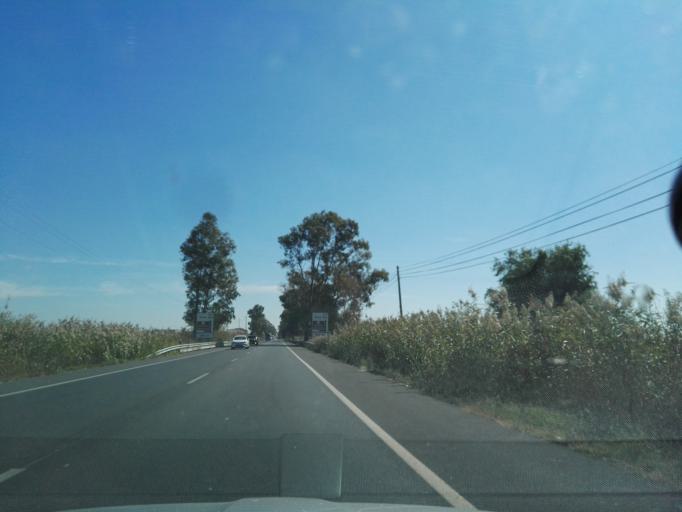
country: PT
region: Lisbon
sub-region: Vila Franca de Xira
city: Vila Franca de Xira
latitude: 38.9444
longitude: -8.9524
